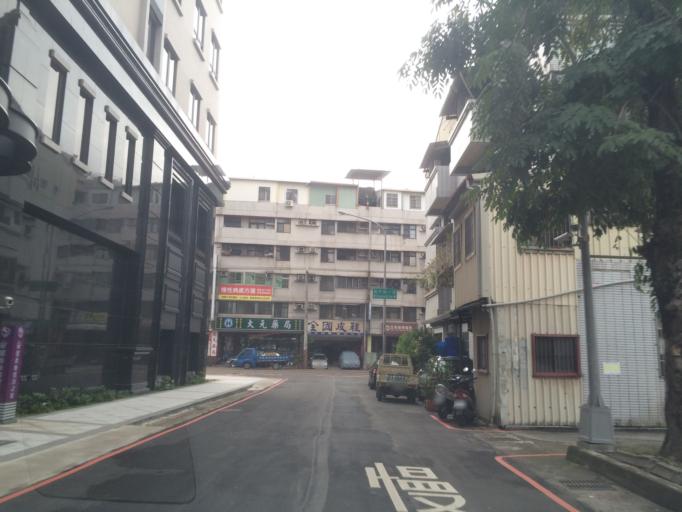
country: TW
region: Taiwan
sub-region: Taichung City
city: Taichung
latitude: 24.1670
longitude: 120.6944
